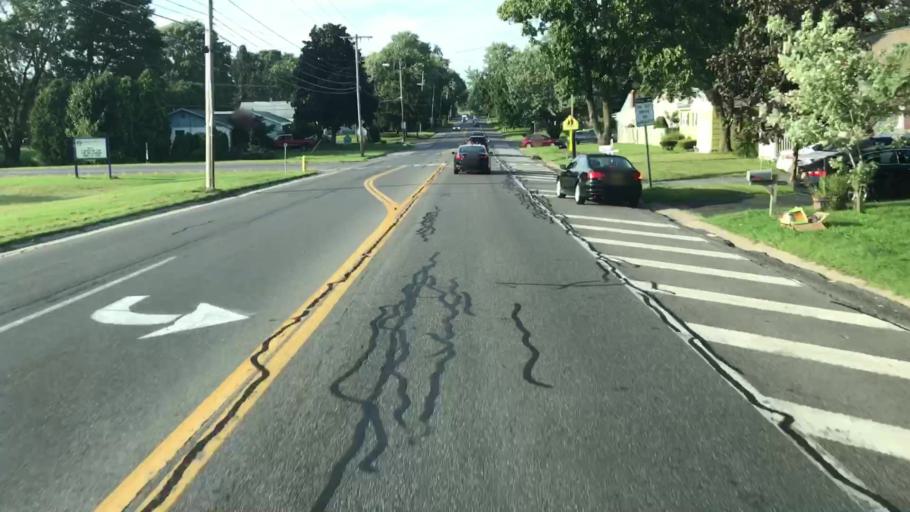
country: US
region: New York
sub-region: Onondaga County
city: Mattydale
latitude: 43.1128
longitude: -76.1598
